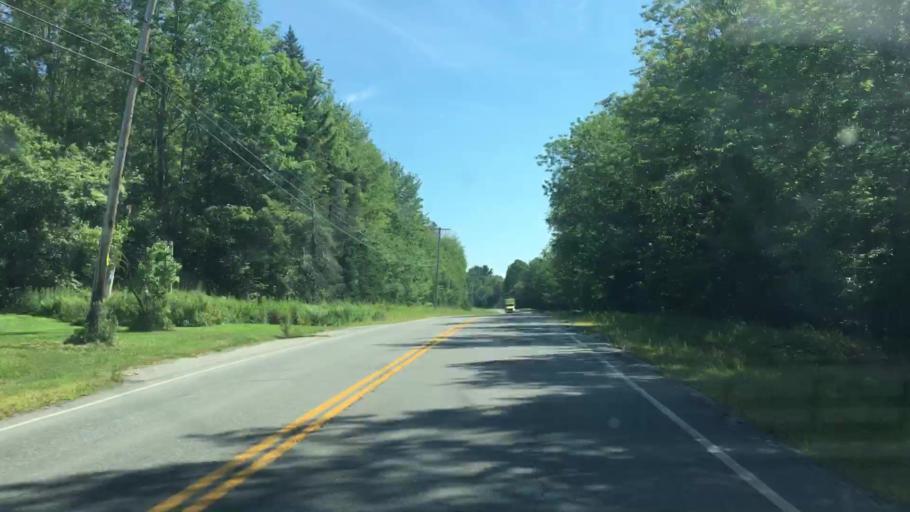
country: US
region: Maine
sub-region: Piscataquis County
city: Milo
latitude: 45.1971
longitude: -68.9040
